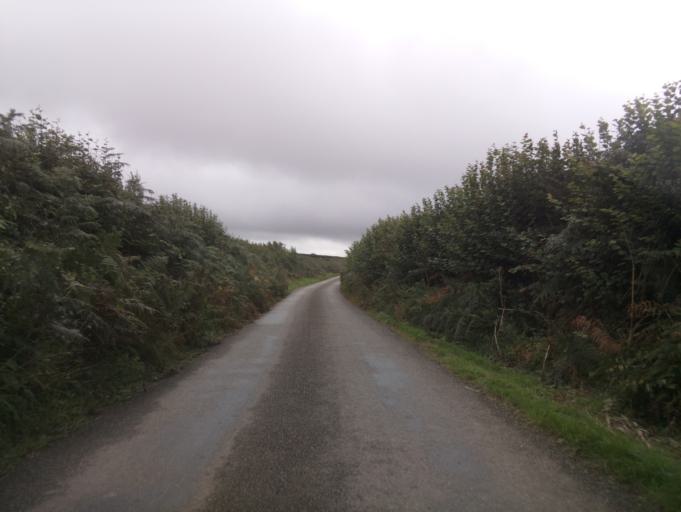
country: GB
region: England
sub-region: Devon
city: Kingsbridge
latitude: 50.3037
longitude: -3.7175
